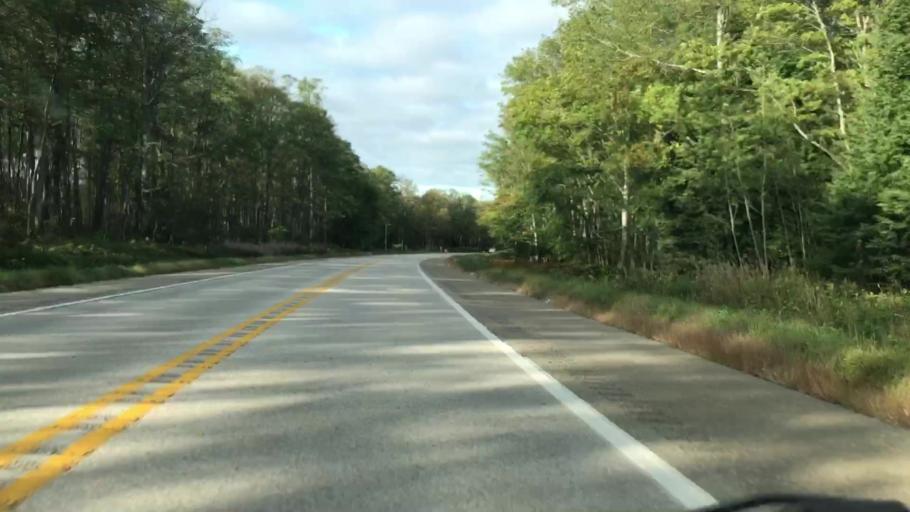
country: US
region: Michigan
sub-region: Luce County
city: Newberry
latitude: 46.3331
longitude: -85.0523
